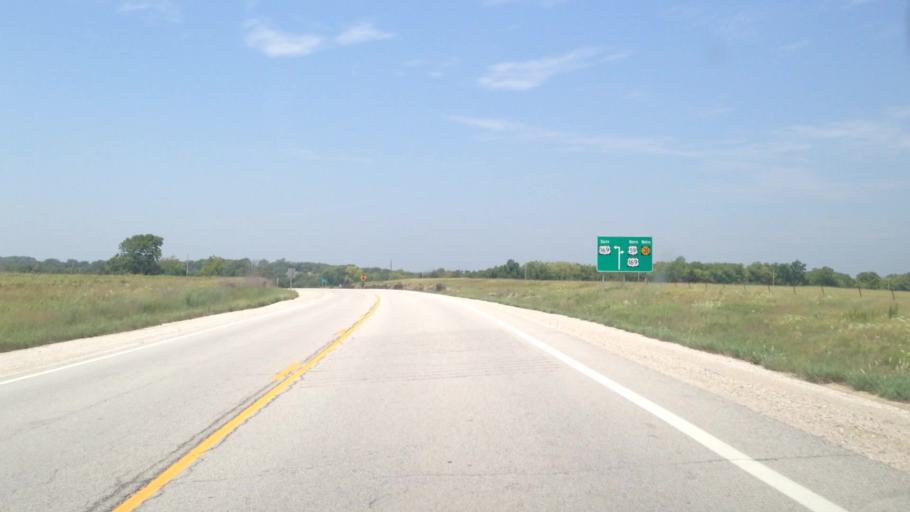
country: US
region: Kansas
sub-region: Anderson County
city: Garnett
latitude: 38.1958
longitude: -95.2461
